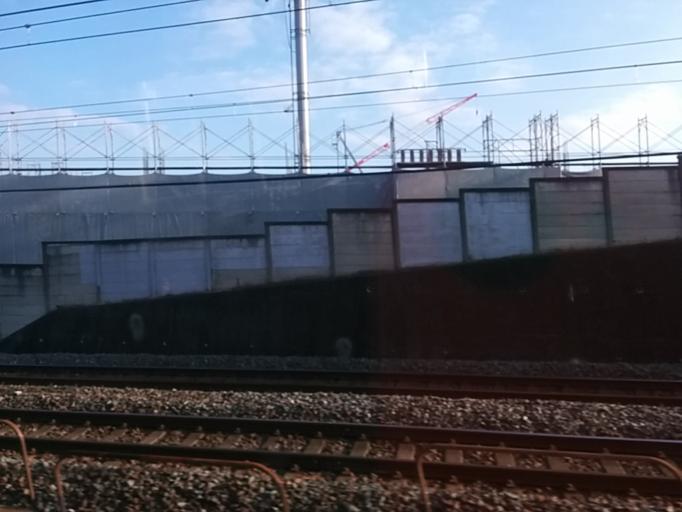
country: JP
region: Saitama
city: Asaka
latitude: 35.8092
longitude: 139.5946
